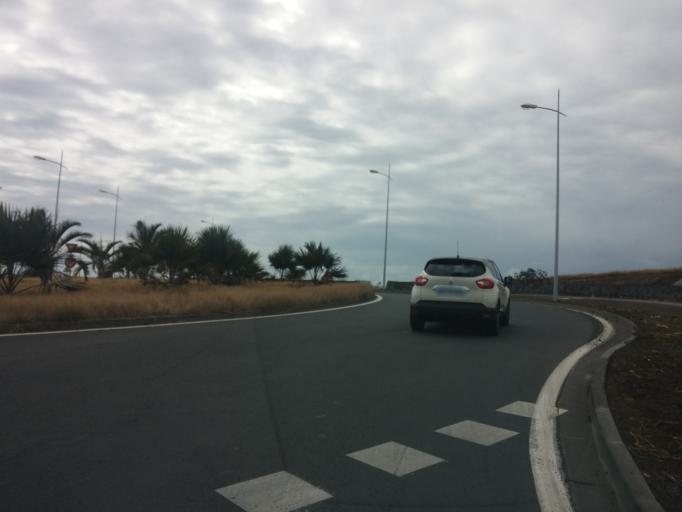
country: RE
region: Reunion
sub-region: Reunion
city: Le Port
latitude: -20.9599
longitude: 55.2938
